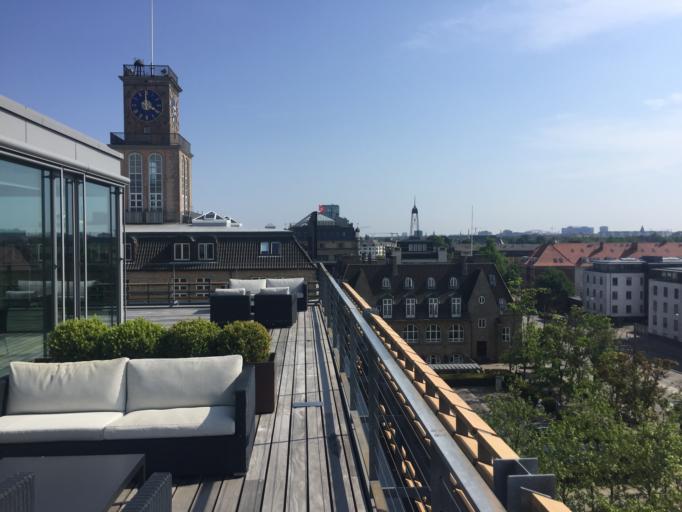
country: DK
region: Capital Region
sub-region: Gentofte Kommune
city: Charlottenlund
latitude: 55.7272
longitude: 12.5771
